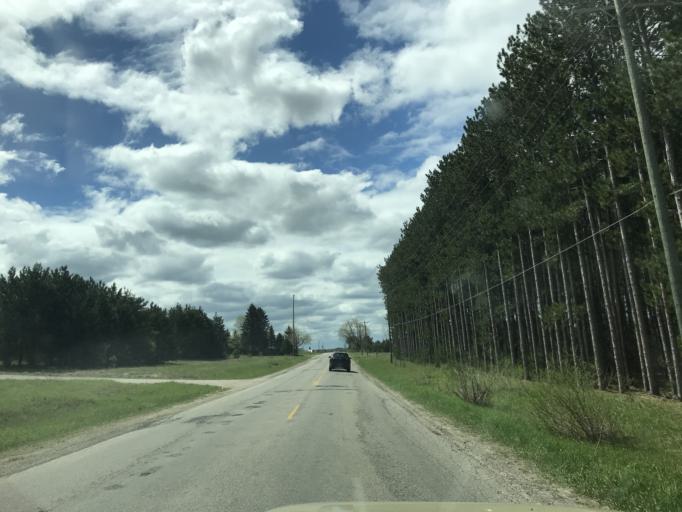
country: US
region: Michigan
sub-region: Otsego County
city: Gaylord
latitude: 45.0363
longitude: -84.6942
